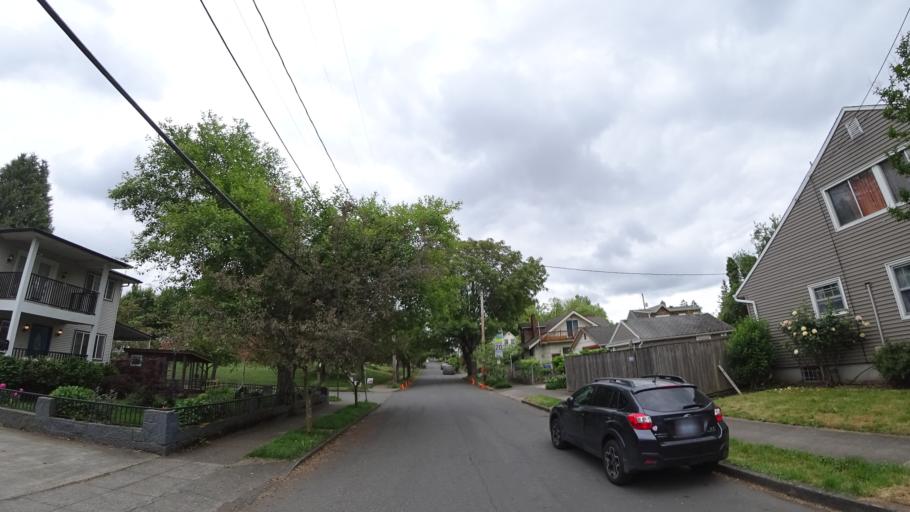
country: US
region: Oregon
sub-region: Multnomah County
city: Lents
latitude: 45.5219
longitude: -122.6049
